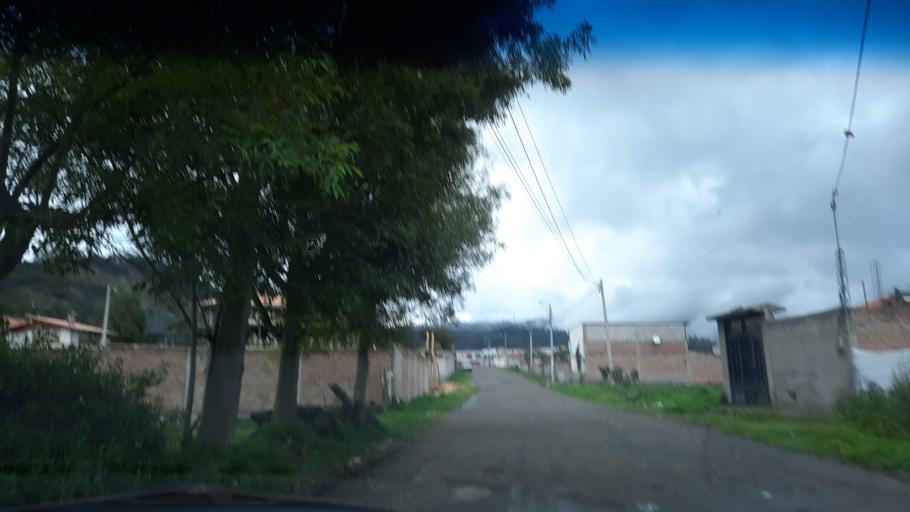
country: EC
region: Chimborazo
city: Riobamba
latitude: -1.6870
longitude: -78.6587
